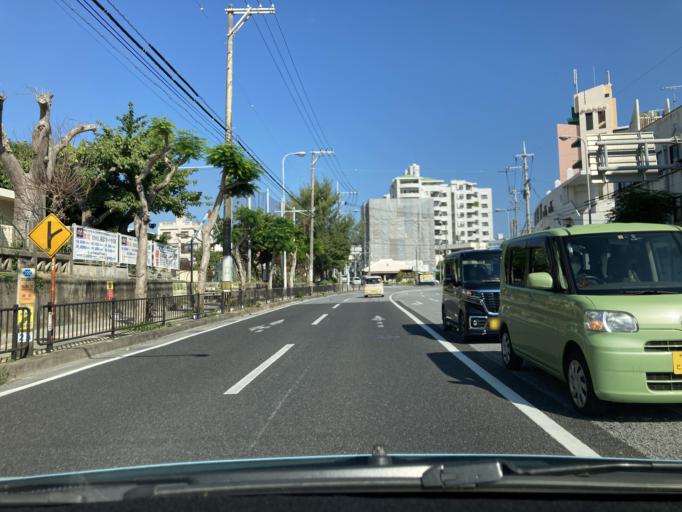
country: JP
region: Okinawa
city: Naha-shi
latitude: 26.2060
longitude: 127.6995
